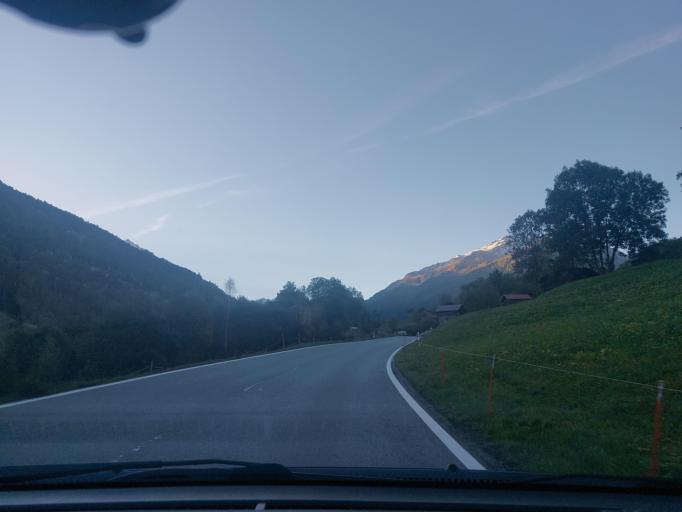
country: CH
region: Valais
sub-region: Sierre District
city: Chippis
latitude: 46.2020
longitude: 7.5854
